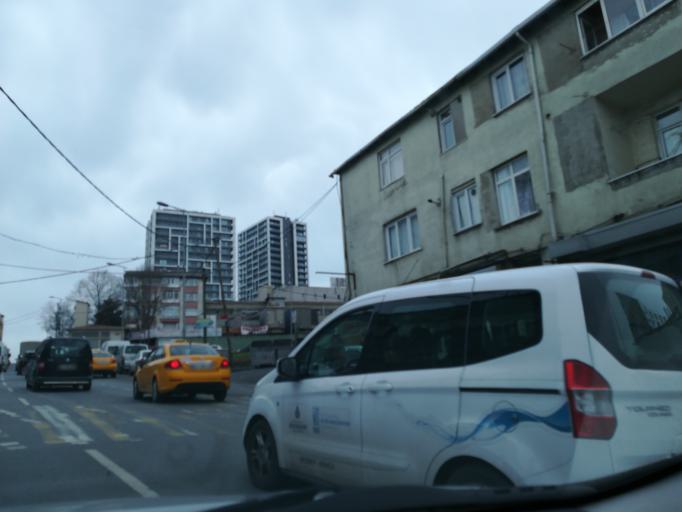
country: TR
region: Istanbul
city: Mahmutbey
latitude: 41.0455
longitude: 28.8270
